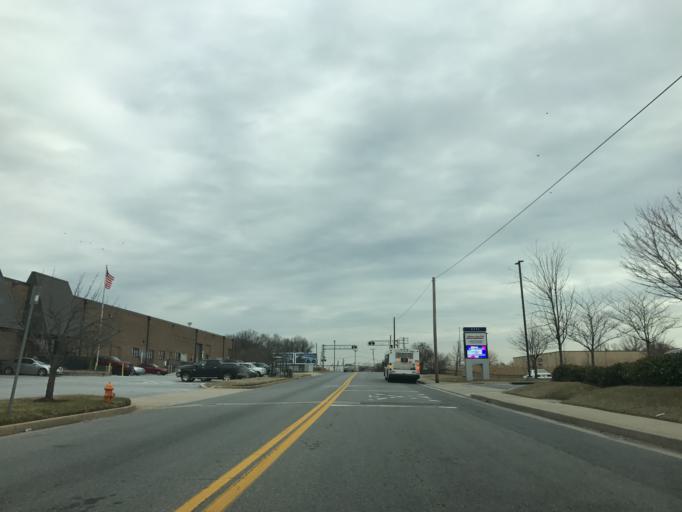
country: US
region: Maryland
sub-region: Baltimore County
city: Lansdowne
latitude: 39.2298
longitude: -76.6813
